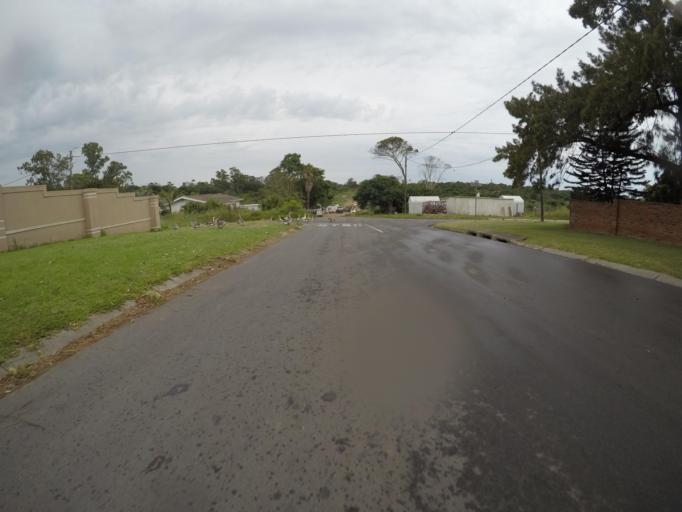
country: ZA
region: Eastern Cape
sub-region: Buffalo City Metropolitan Municipality
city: East London
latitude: -32.9664
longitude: 27.8360
